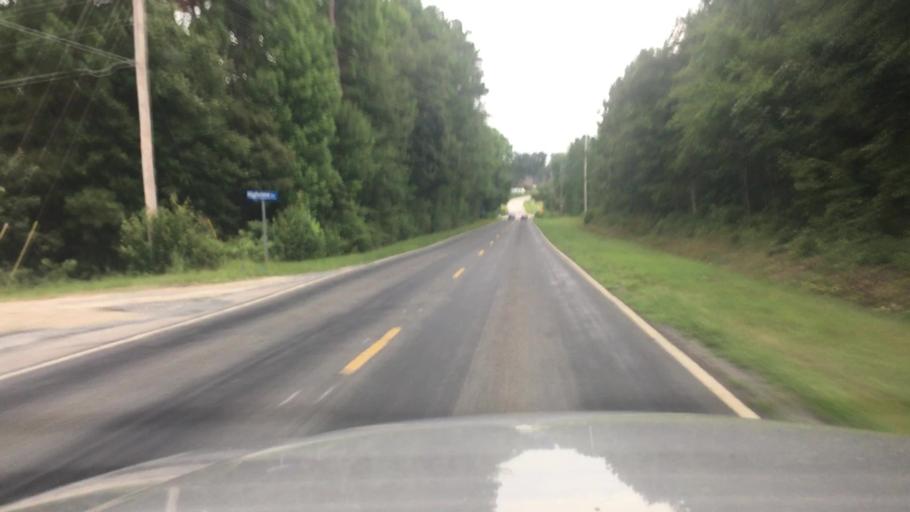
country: US
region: North Carolina
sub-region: Hoke County
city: Rockfish
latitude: 34.9805
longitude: -79.0512
